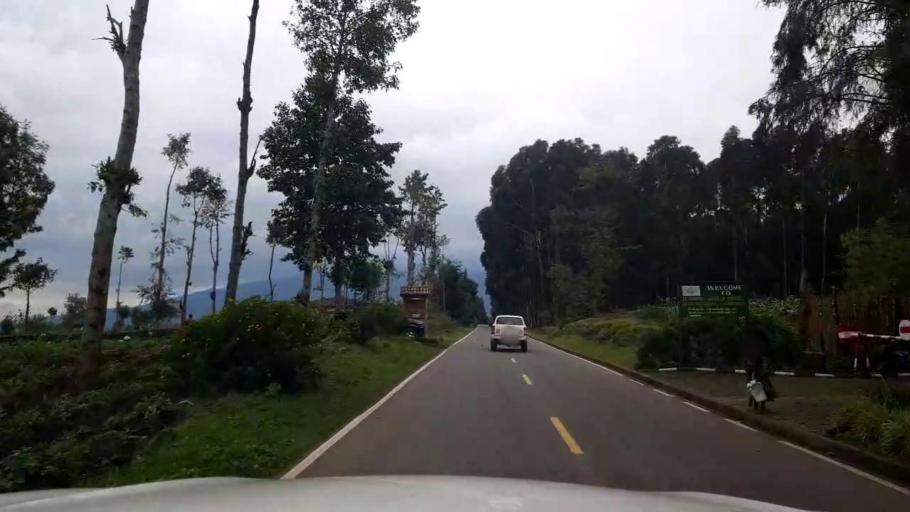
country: RW
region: Northern Province
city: Musanze
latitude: -1.4318
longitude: 29.5596
